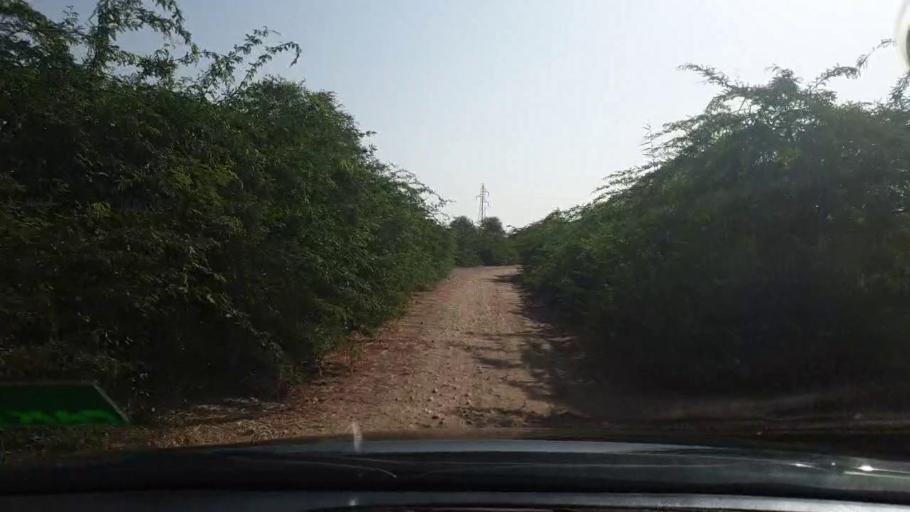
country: PK
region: Sindh
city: Tando Bago
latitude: 24.7246
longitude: 68.9557
